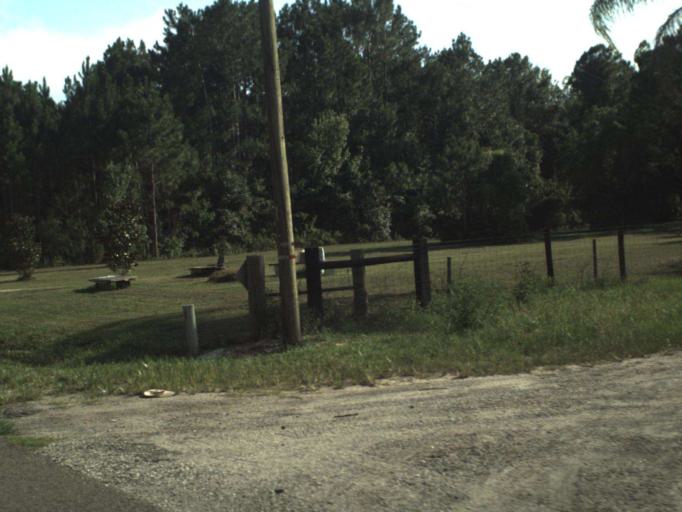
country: US
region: Florida
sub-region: Lake County
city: Groveland
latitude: 28.4545
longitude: -81.8335
